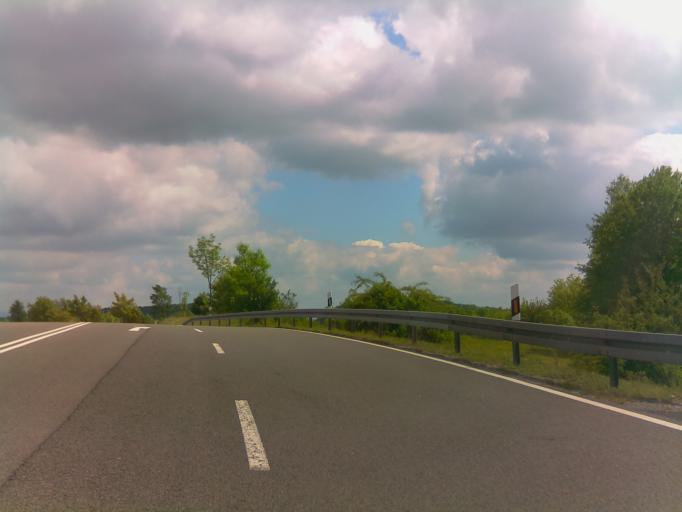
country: DE
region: Thuringia
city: Henneberg
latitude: 50.4847
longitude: 10.3394
